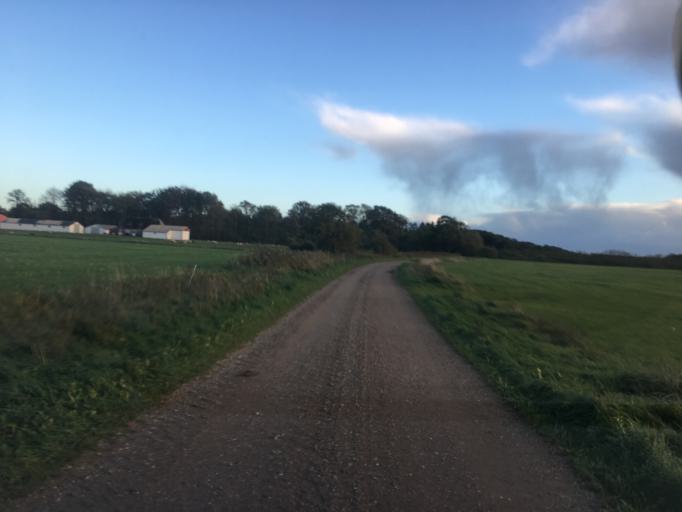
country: DE
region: Schleswig-Holstein
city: Ellhoft
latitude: 54.9419
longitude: 9.0101
